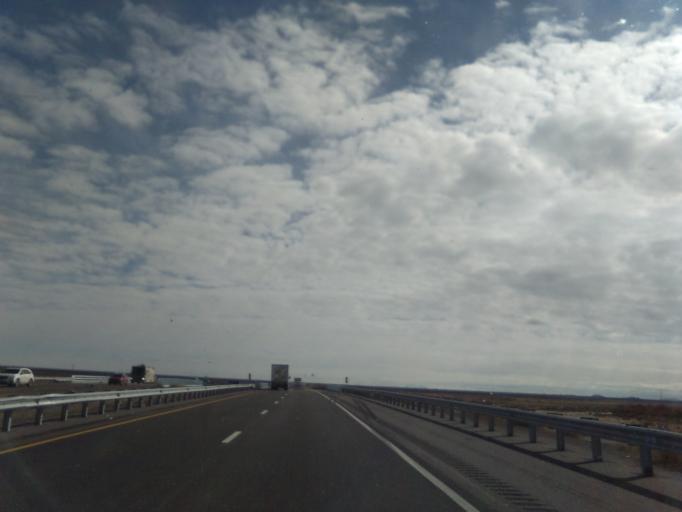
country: US
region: New Mexico
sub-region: Hidalgo County
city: Lordsburg
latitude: 32.3125
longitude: -108.6087
